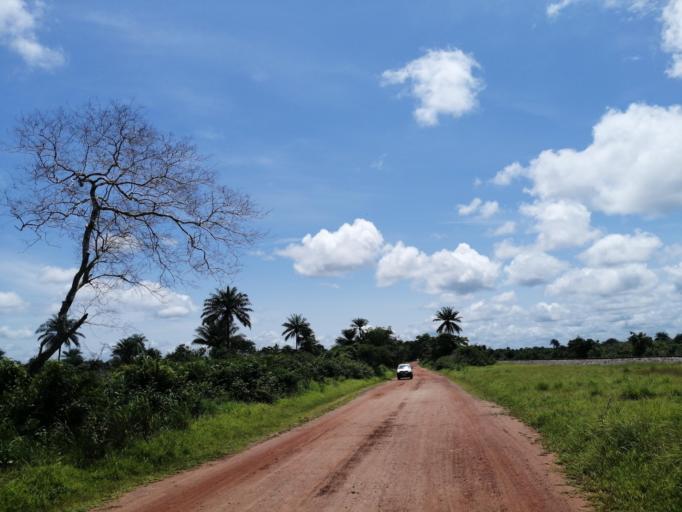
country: SL
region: Northern Province
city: Pepel
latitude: 8.6603
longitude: -13.0041
